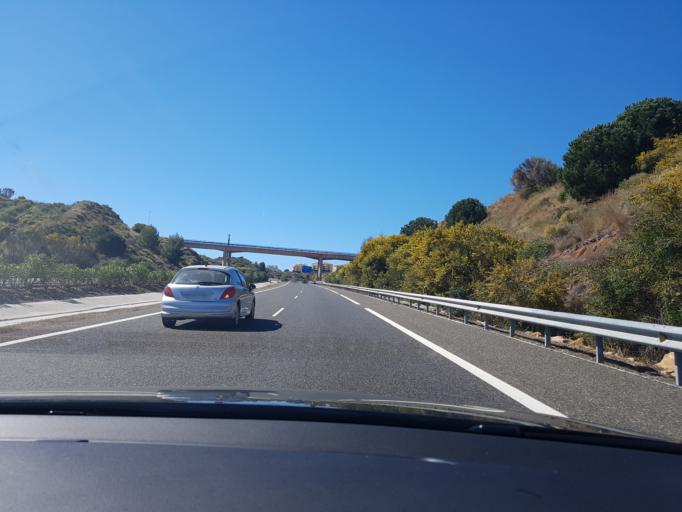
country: ES
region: Andalusia
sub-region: Provincia de Malaga
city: Fuengirola
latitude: 36.5113
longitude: -4.7055
